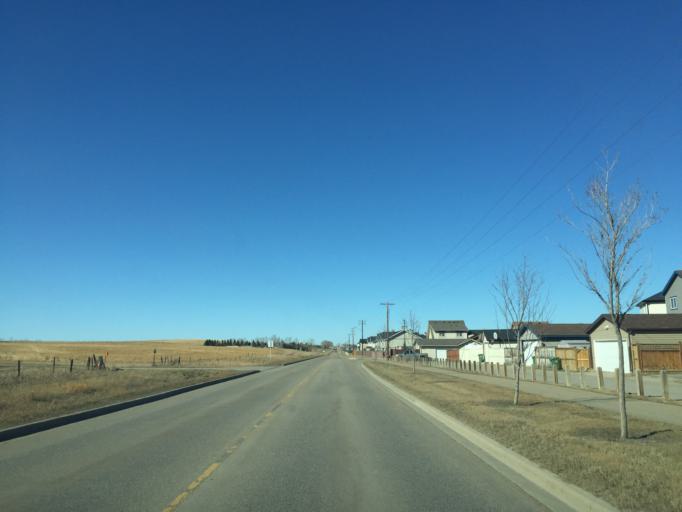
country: CA
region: Alberta
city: Airdrie
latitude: 51.2895
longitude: -114.0485
